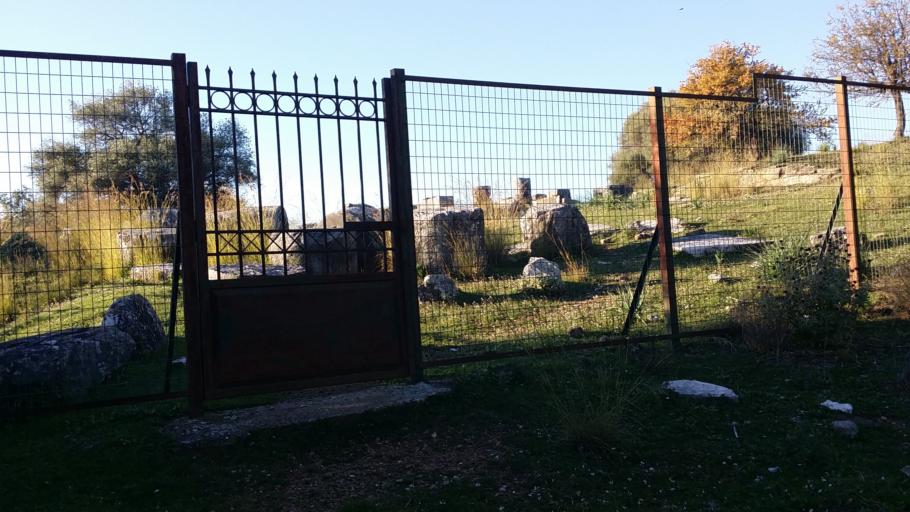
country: GR
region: West Greece
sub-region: Nomos Aitolias kai Akarnanias
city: Lepenou
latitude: 38.6708
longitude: 21.3116
